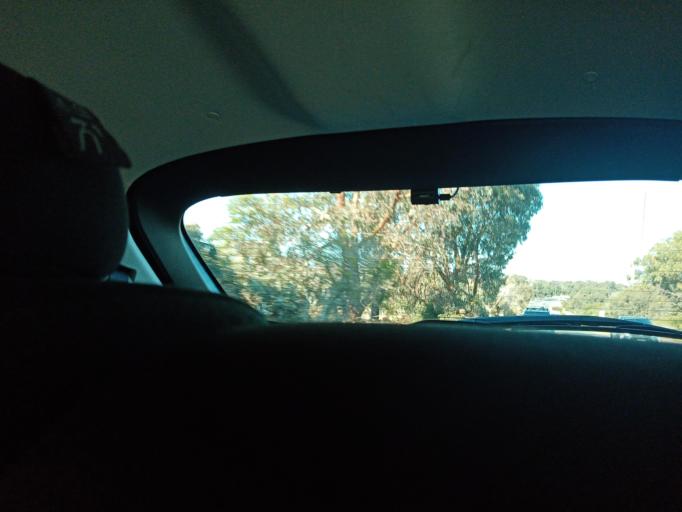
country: AU
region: Western Australia
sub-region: City of Cockburn
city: Yangebup
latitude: -32.1268
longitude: 115.8293
